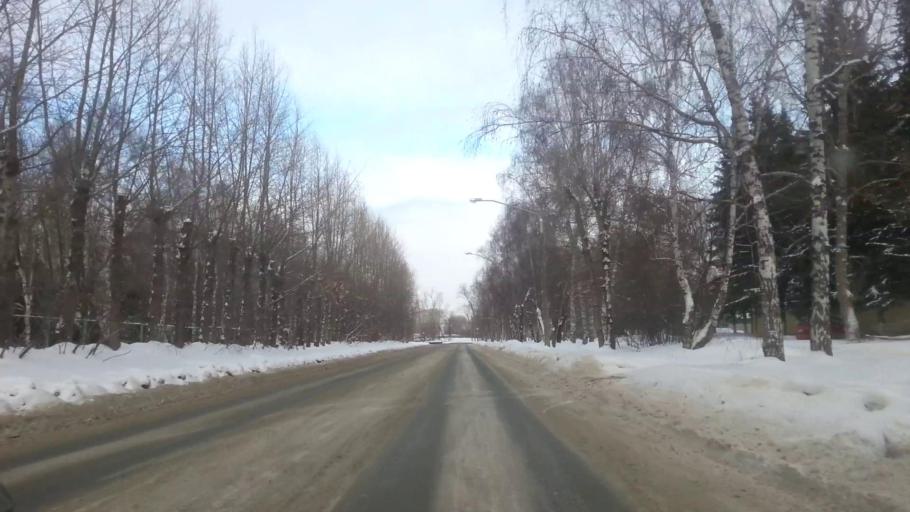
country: RU
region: Altai Krai
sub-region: Gorod Barnaulskiy
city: Barnaul
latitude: 53.3680
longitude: 83.6935
